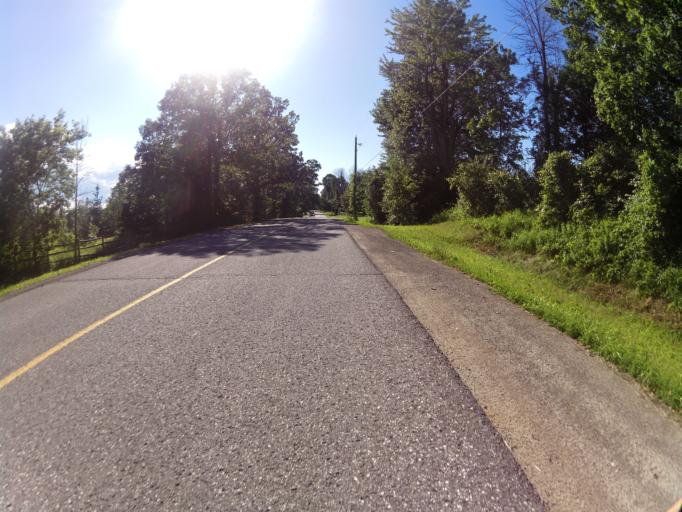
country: CA
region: Ontario
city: Bells Corners
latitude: 45.2643
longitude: -75.8180
